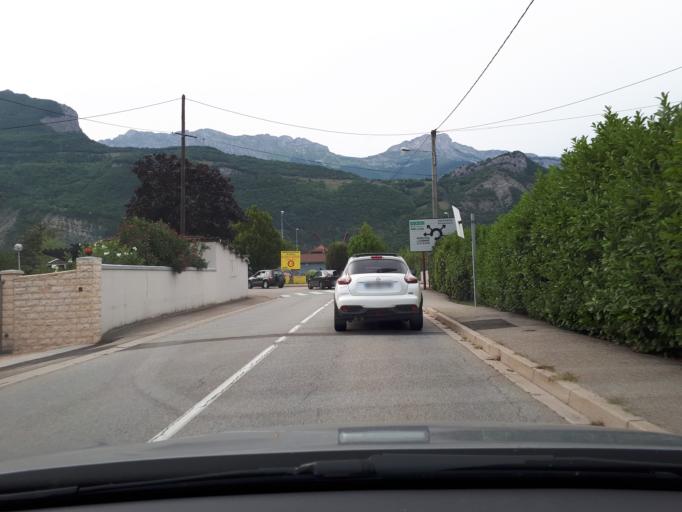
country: FR
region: Rhone-Alpes
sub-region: Departement de l'Isere
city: Vif
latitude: 45.0523
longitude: 5.6782
